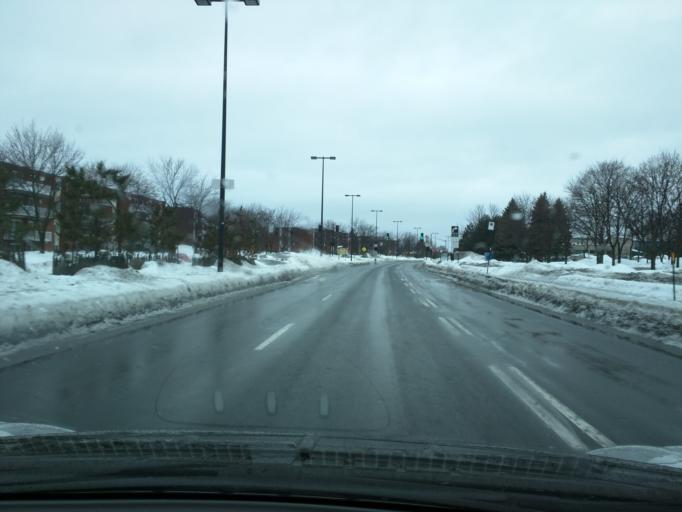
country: CA
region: Quebec
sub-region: Monteregie
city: Longueuil
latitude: 45.5329
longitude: -73.4627
